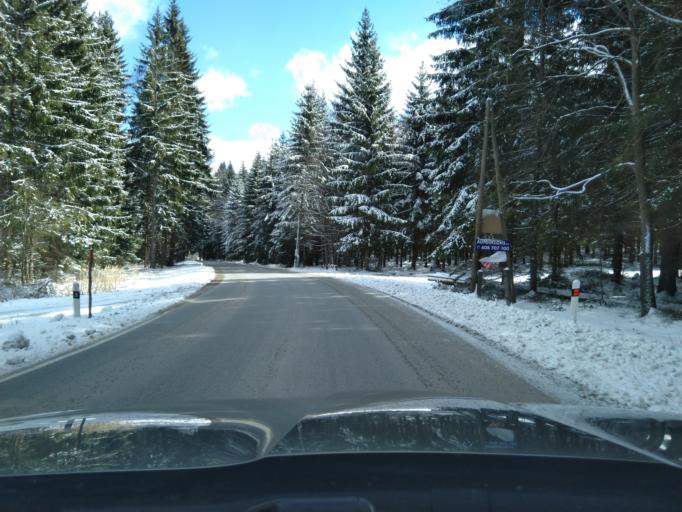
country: CZ
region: Jihocesky
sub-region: Okres Prachatice
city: Zdikov
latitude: 49.0595
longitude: 13.7192
